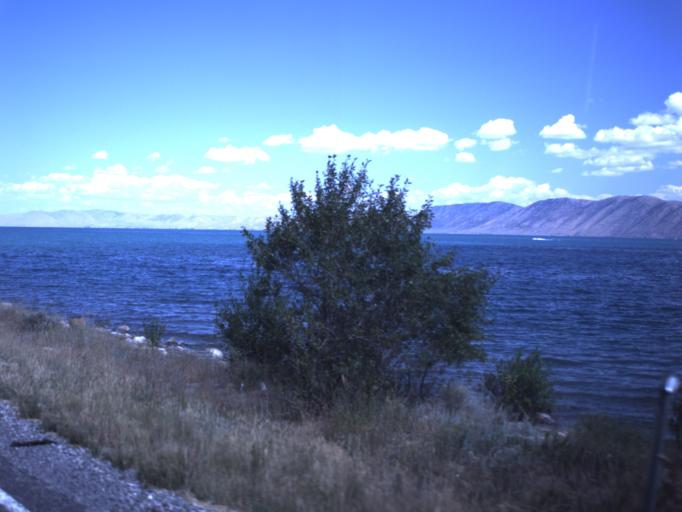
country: US
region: Utah
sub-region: Rich County
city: Randolph
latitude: 41.8953
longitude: -111.3664
